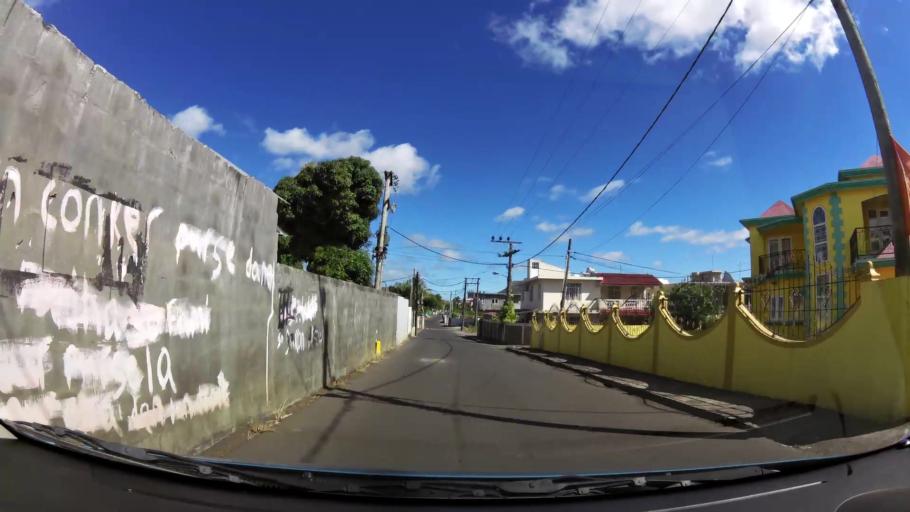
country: MU
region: Plaines Wilhems
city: Vacoas
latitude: -20.2906
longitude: 57.4756
